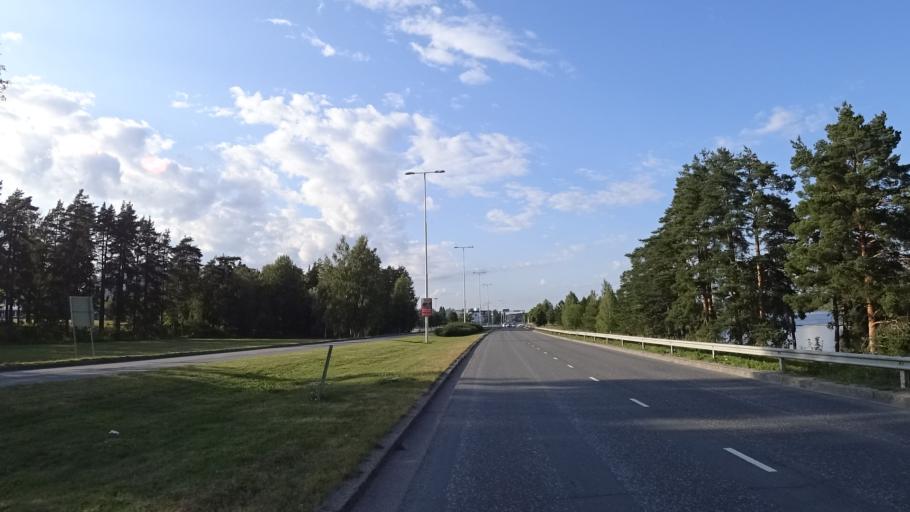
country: FI
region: South Karelia
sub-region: Imatra
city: Imatra
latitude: 61.1864
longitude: 28.7781
